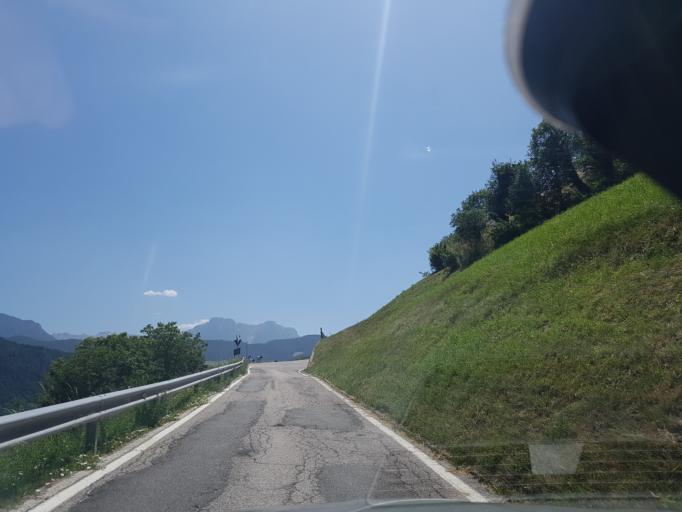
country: IT
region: Trentino-Alto Adige
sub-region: Bolzano
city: Villandro - Villanders
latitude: 46.6230
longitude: 11.5350
